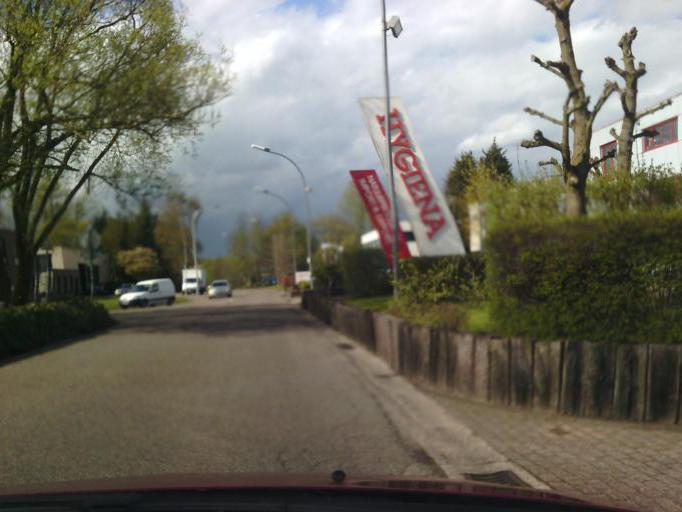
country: BE
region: Flanders
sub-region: Provincie Oost-Vlaanderen
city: Sint-Niklaas
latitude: 51.1431
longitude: 4.1748
